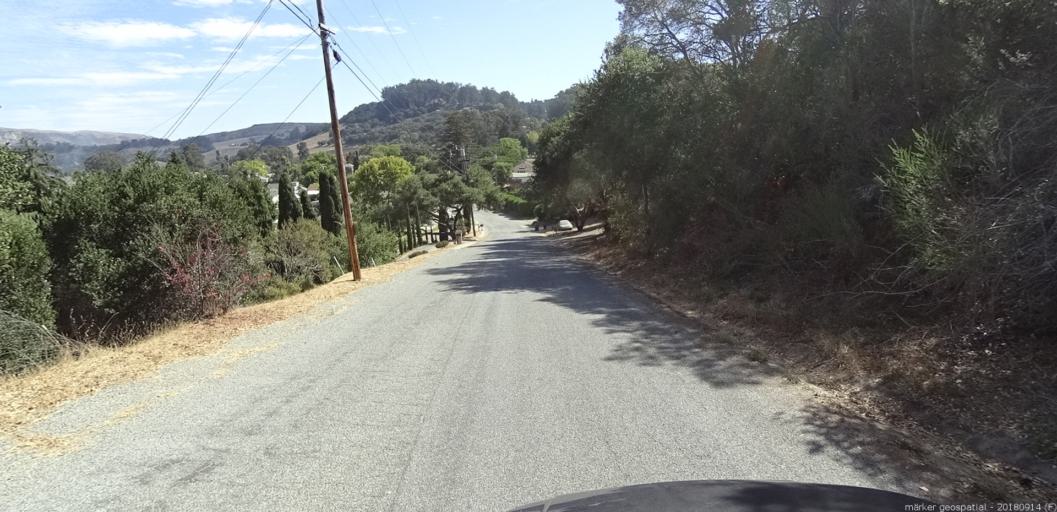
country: US
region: California
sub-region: San Benito County
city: Aromas
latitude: 36.8856
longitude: -121.6447
